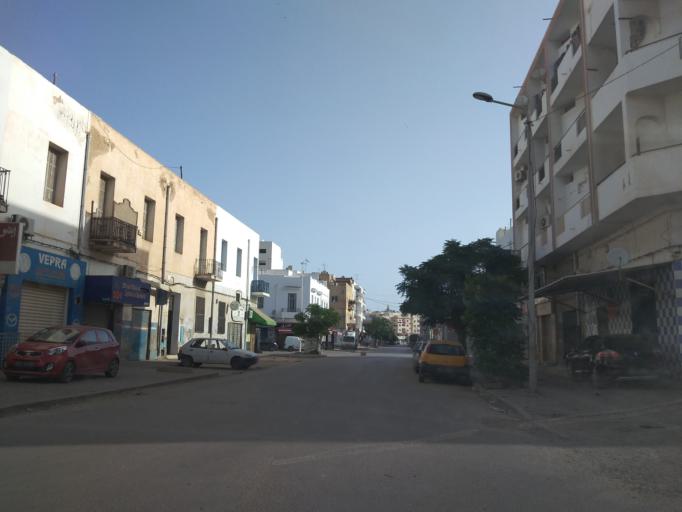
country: TN
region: Safaqis
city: Sfax
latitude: 34.7316
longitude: 10.7548
